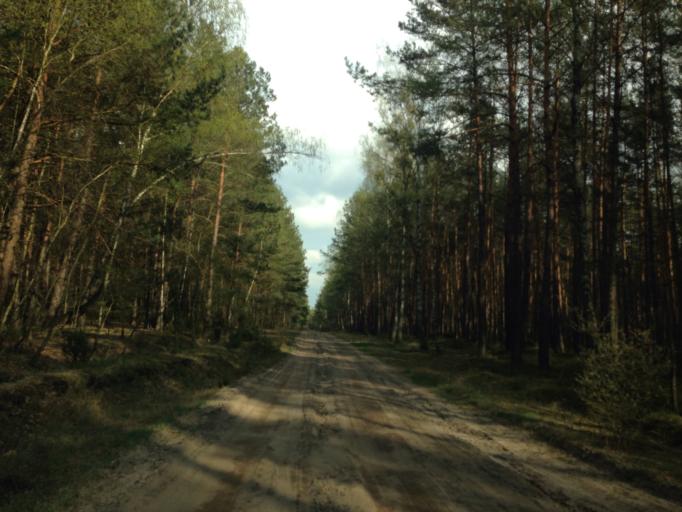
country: PL
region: Kujawsko-Pomorskie
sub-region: Powiat brodnicki
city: Gorzno
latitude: 53.1263
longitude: 19.6855
